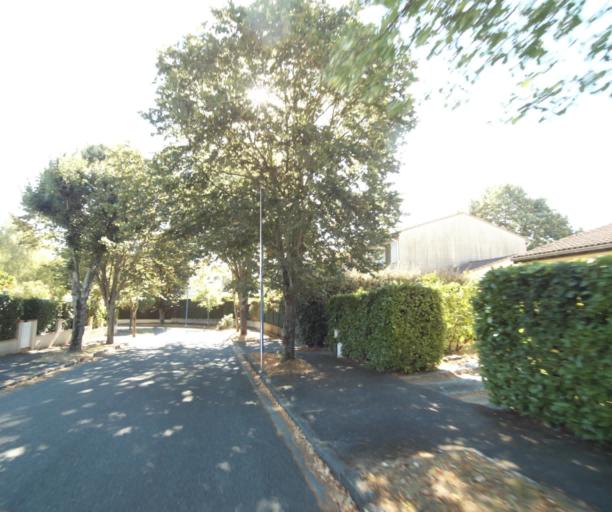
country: FR
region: Midi-Pyrenees
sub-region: Departement de la Haute-Garonne
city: Castanet-Tolosan
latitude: 43.5226
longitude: 1.5117
